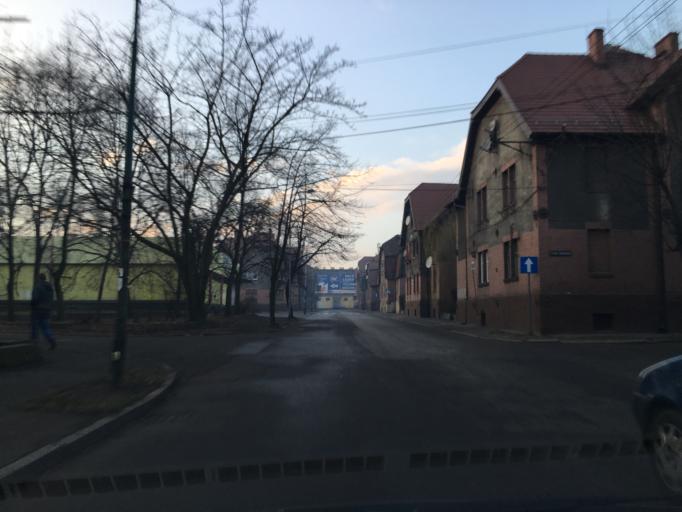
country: PL
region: Silesian Voivodeship
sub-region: Bytom
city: Bytom
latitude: 50.3396
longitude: 18.8727
